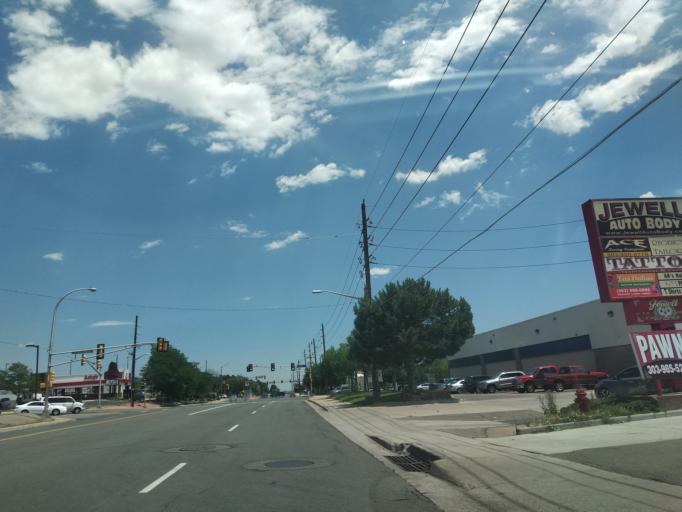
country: US
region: Colorado
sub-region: Jefferson County
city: Lakewood
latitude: 39.6821
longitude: -105.0840
